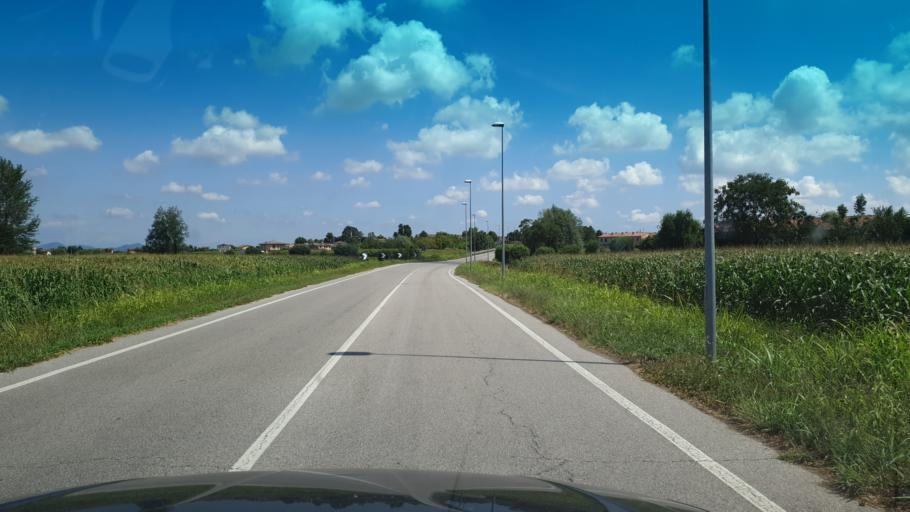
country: IT
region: Veneto
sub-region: Provincia di Rovigo
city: Costa di Rovigo
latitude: 45.0531
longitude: 11.6917
